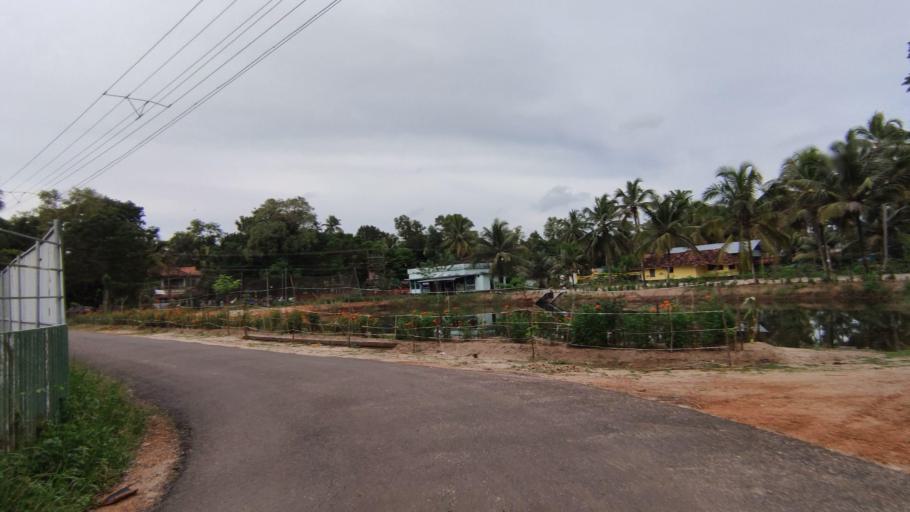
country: IN
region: Kerala
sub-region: Alappuzha
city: Shertallai
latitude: 9.6386
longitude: 76.3610
